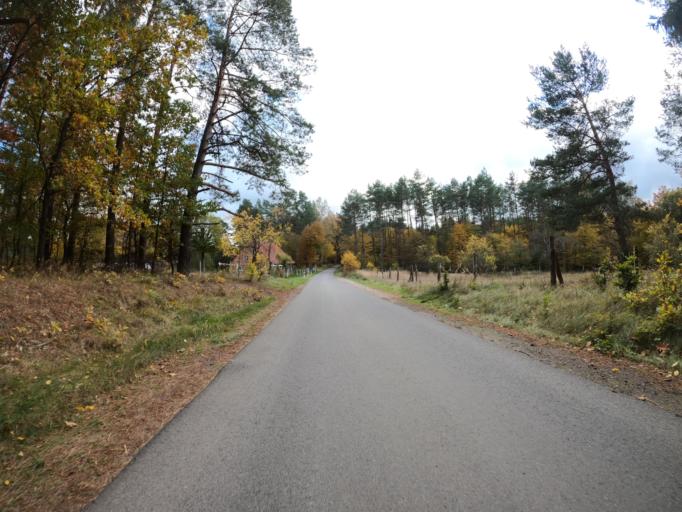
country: PL
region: West Pomeranian Voivodeship
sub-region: Powiat mysliborski
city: Barlinek
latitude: 52.9331
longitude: 15.2853
